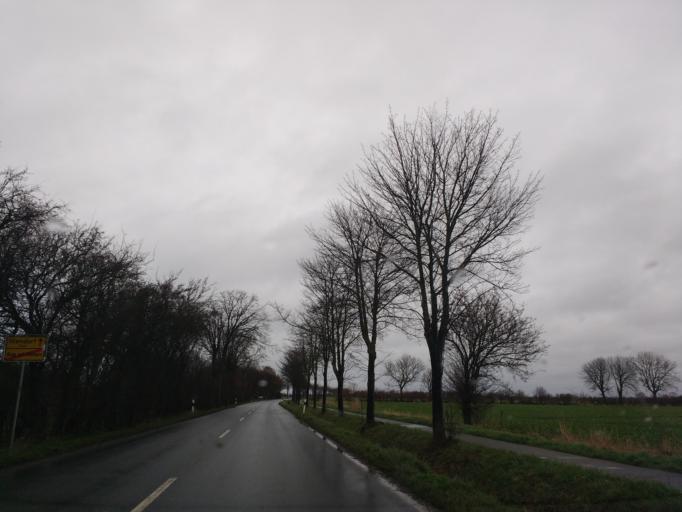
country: DE
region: Schleswig-Holstein
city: Fehmarn
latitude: 54.4461
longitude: 11.2002
